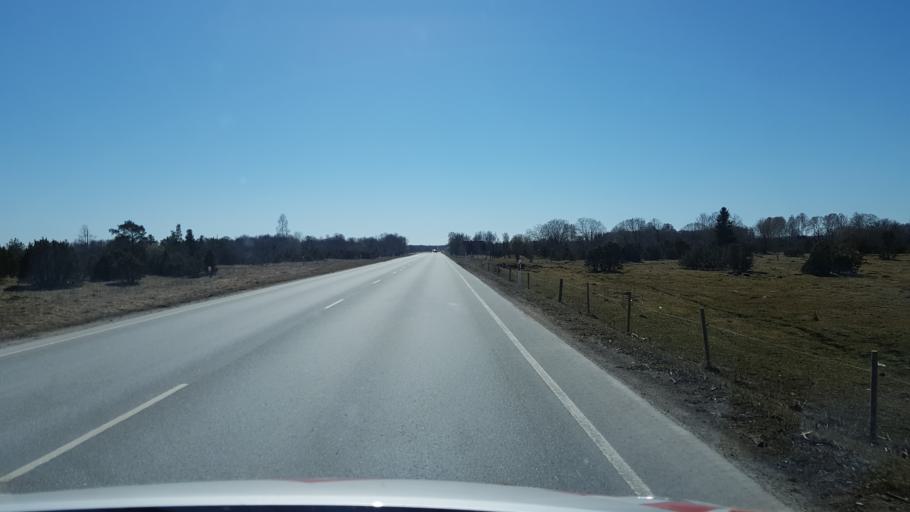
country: EE
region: Laeaene-Virumaa
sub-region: Viru-Nigula vald
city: Kunda
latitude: 59.4753
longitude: 26.4841
